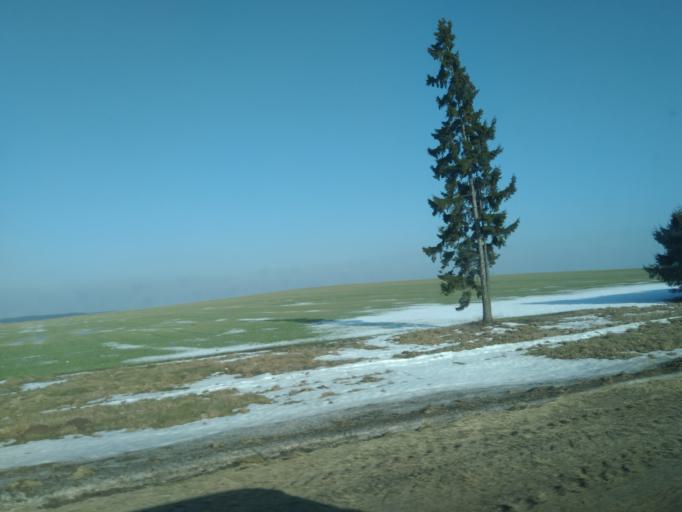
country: BY
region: Minsk
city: Snow
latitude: 53.2122
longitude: 26.4602
